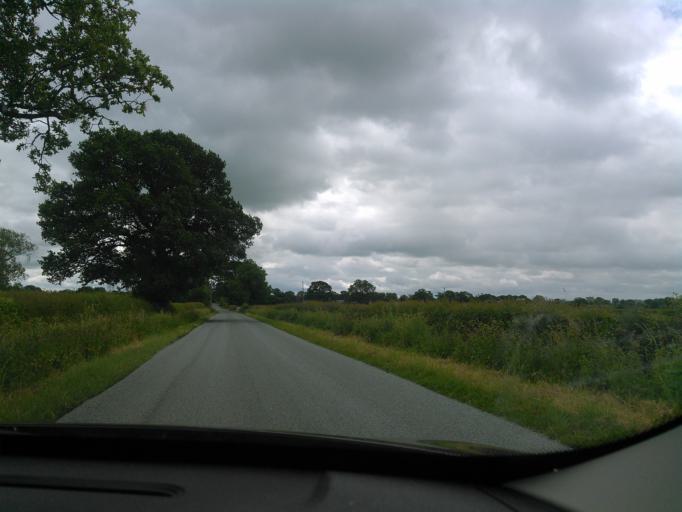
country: GB
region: England
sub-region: Shropshire
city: Wem
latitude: 52.8963
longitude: -2.7604
